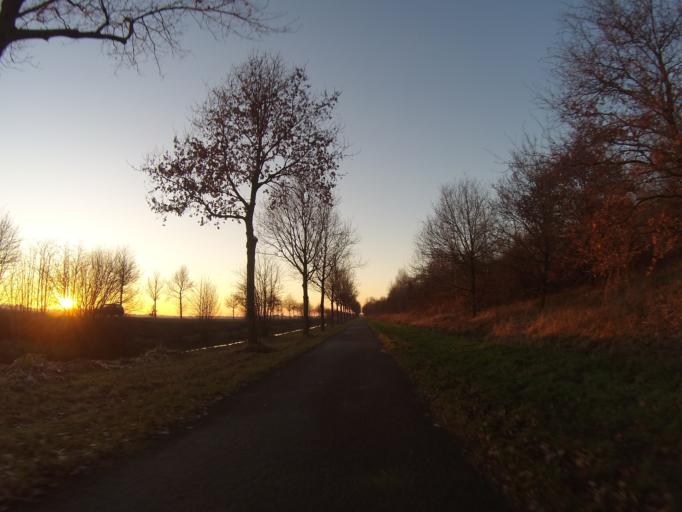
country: NL
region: Drenthe
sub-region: Gemeente Emmen
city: Emmen
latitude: 52.7251
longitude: 6.9010
